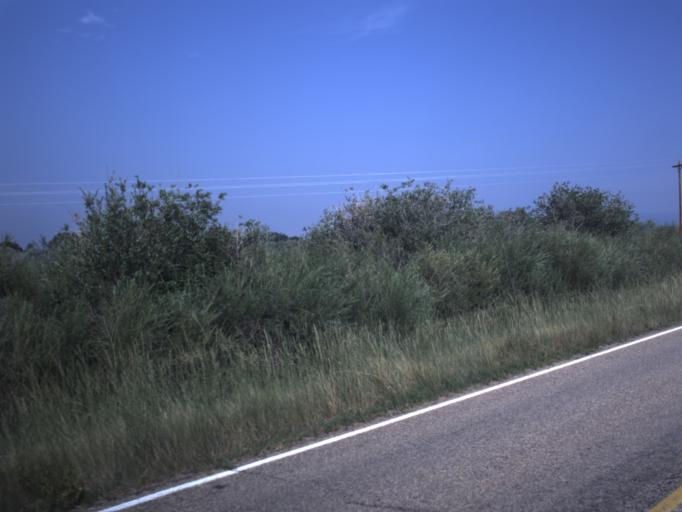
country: US
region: Utah
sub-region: Duchesne County
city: Duchesne
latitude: 40.3178
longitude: -110.2554
